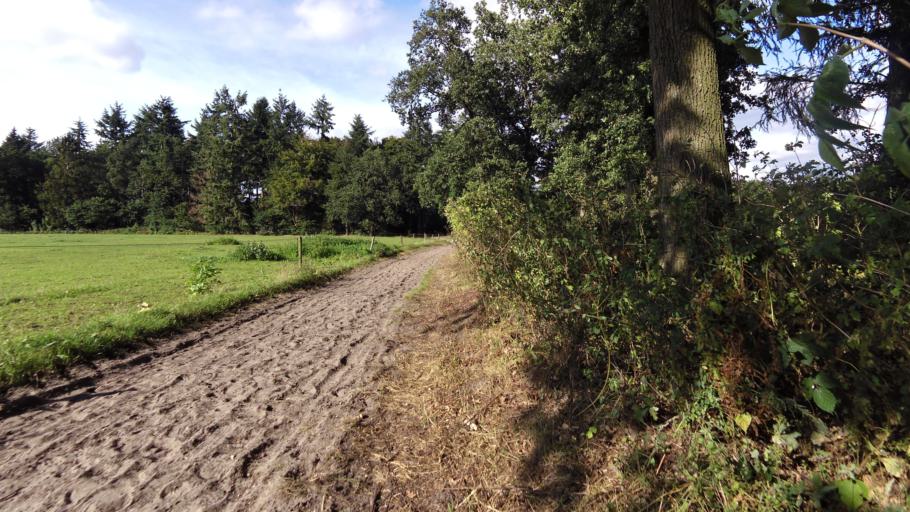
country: NL
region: Gelderland
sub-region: Gemeente Renkum
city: Renkum
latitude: 51.9978
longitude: 5.7314
